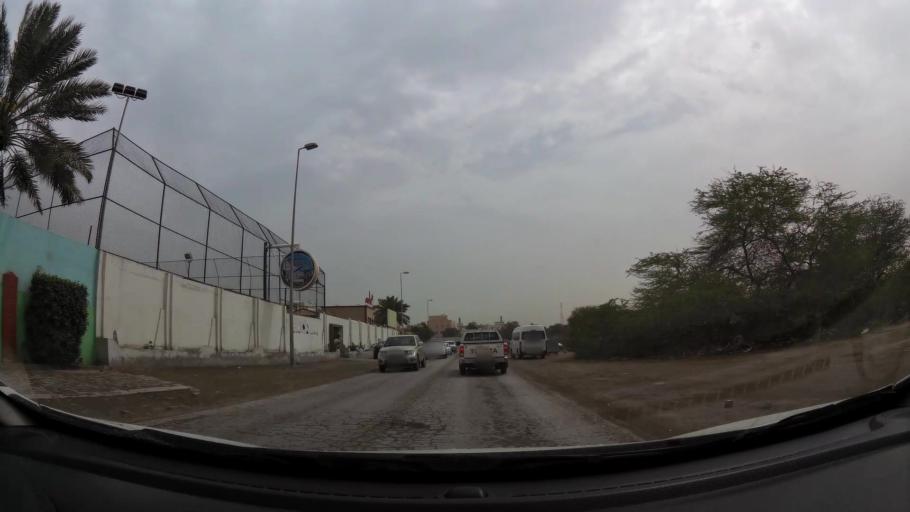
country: BH
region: Northern
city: Ar Rifa'
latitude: 26.1328
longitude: 50.5905
